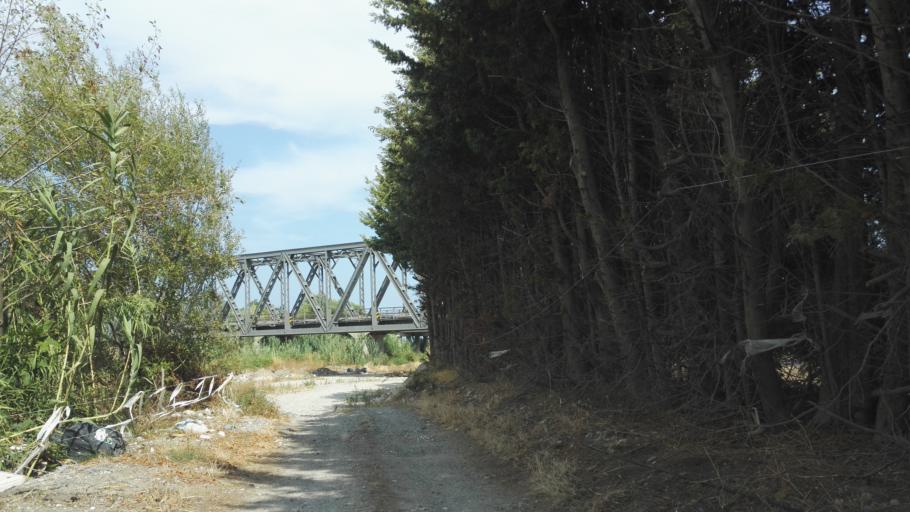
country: IT
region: Calabria
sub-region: Provincia di Reggio Calabria
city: Monasterace Marina
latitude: 38.4270
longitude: 16.5680
